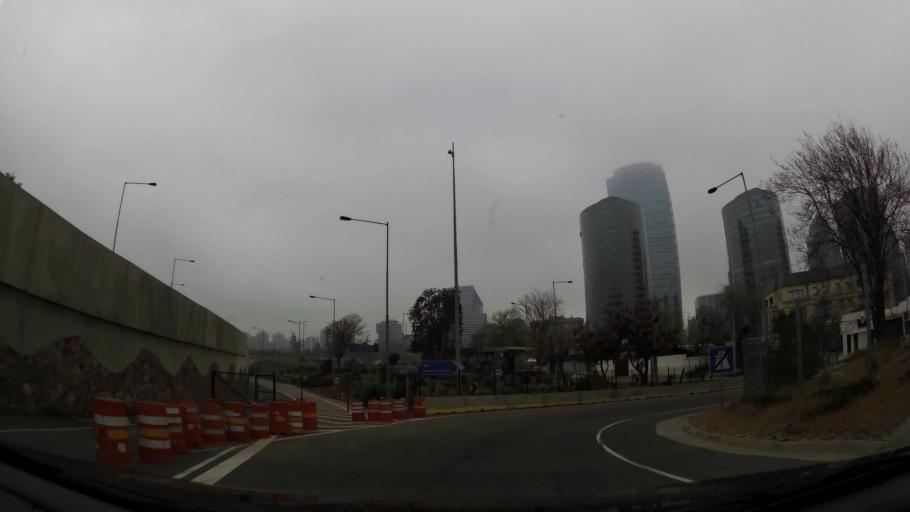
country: CL
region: Santiago Metropolitan
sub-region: Provincia de Santiago
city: Villa Presidente Frei, Nunoa, Santiago, Chile
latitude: -33.4124
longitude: -70.6085
